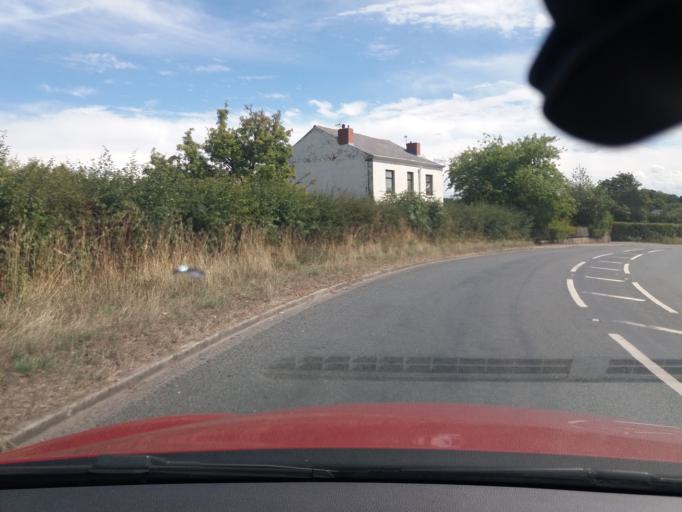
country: GB
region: England
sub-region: Lancashire
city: Euxton
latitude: 53.6632
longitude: -2.7084
